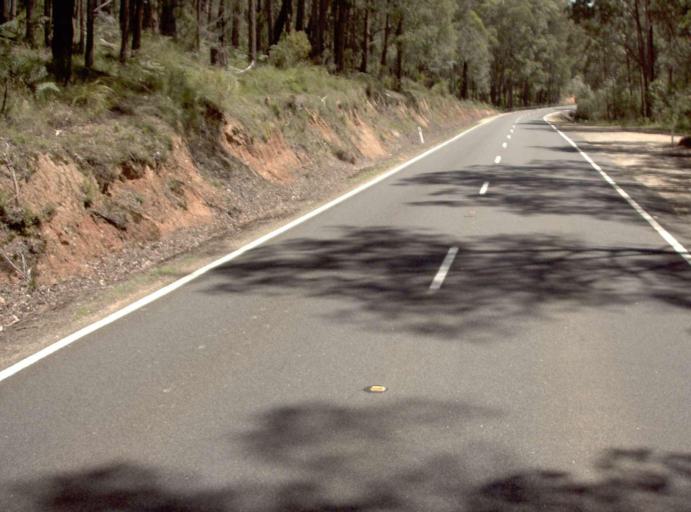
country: AU
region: New South Wales
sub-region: Bombala
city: Bombala
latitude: -37.5939
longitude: 148.9148
